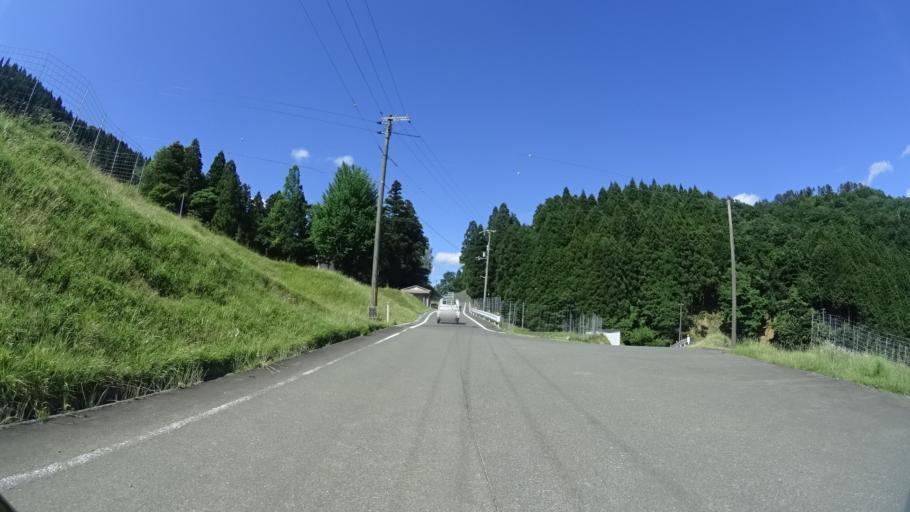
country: JP
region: Kyoto
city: Fukuchiyama
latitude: 35.3903
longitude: 135.0707
